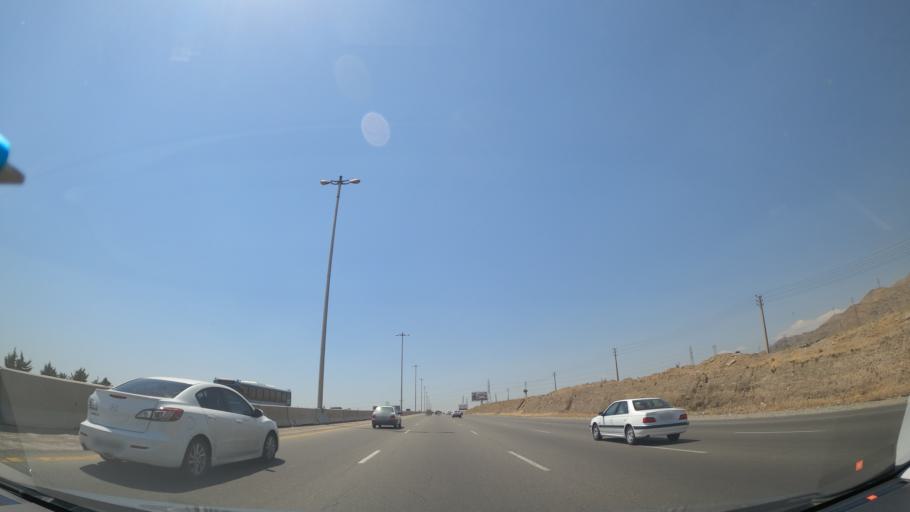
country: IR
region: Tehran
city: Shahr-e Qods
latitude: 35.7675
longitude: 51.0519
